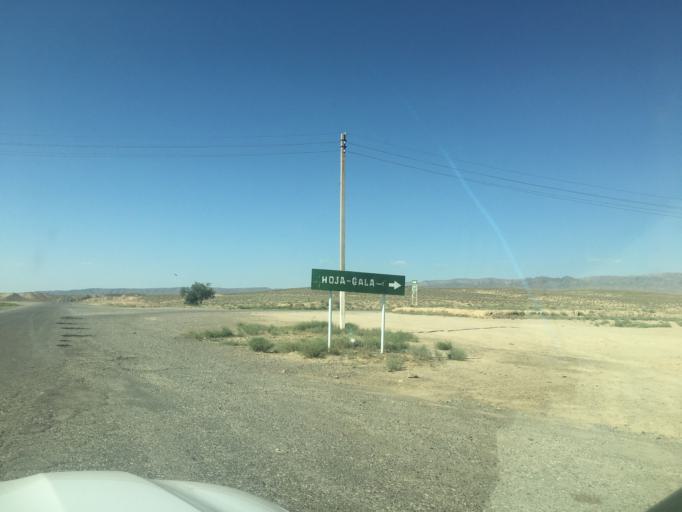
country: TM
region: Balkan
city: Serdar
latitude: 38.7216
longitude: 56.2934
